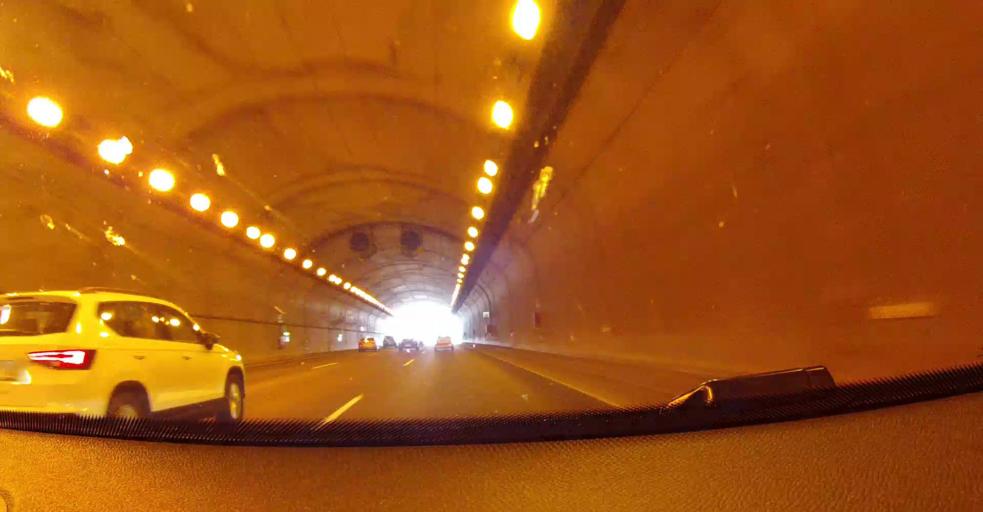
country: ES
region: Basque Country
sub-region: Provincia de Alava
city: Arminon
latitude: 42.7860
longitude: -2.8237
